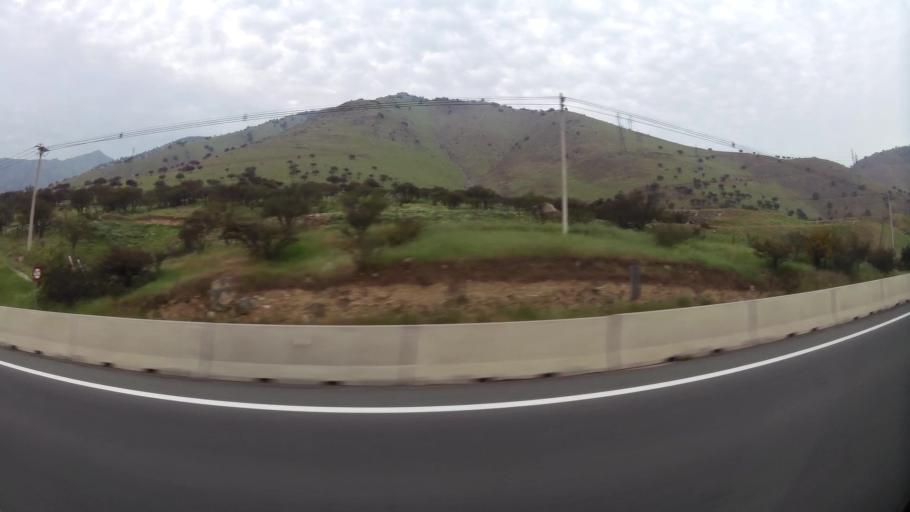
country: CL
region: Santiago Metropolitan
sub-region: Provincia de Chacabuco
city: Chicureo Abajo
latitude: -33.3596
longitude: -70.6167
